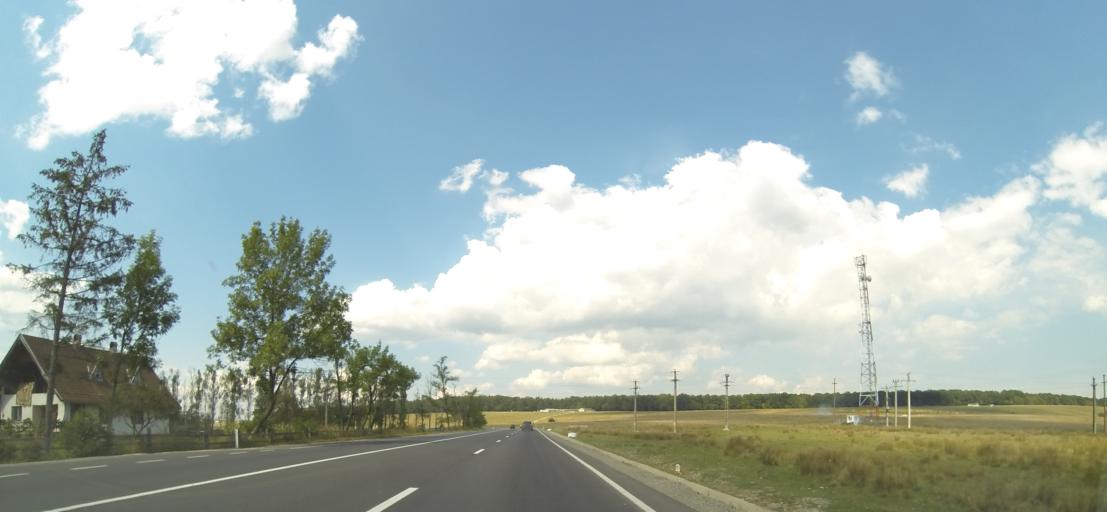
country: RO
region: Brasov
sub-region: Comuna Dumbravita
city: Dumbravita
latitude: 45.7450
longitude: 25.4142
